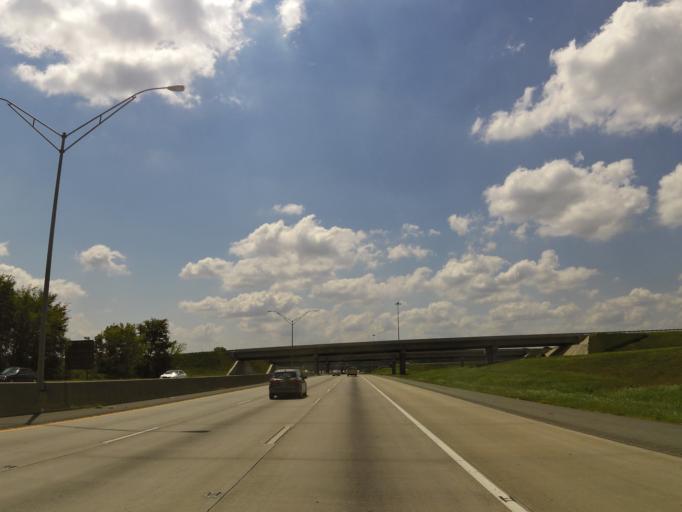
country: US
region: North Carolina
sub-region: Cabarrus County
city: Harrisburg
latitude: 35.3522
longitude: -80.7299
